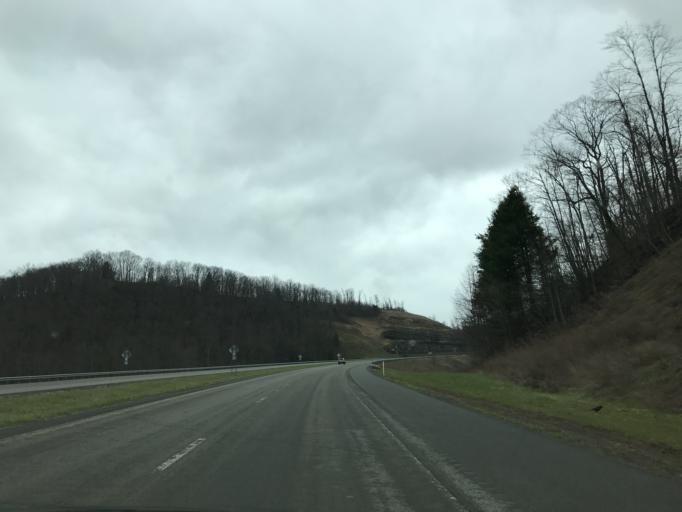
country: US
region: West Virginia
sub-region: Raleigh County
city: Sophia
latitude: 37.7049
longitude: -81.3062
